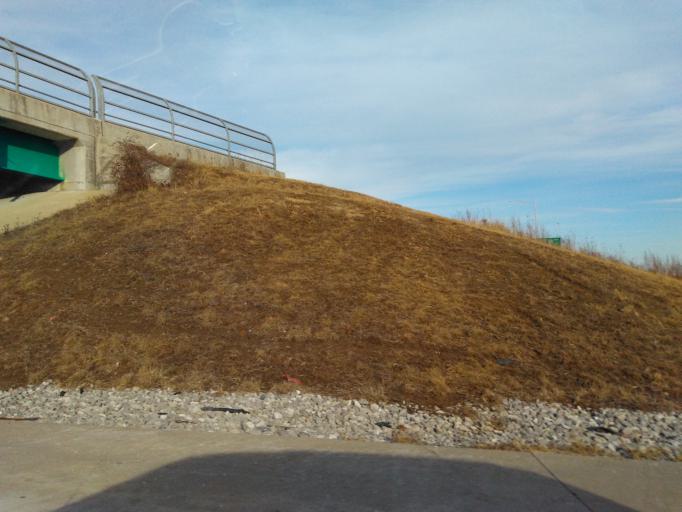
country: US
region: Illinois
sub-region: Jefferson County
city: Mount Vernon
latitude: 38.2995
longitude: -88.9461
